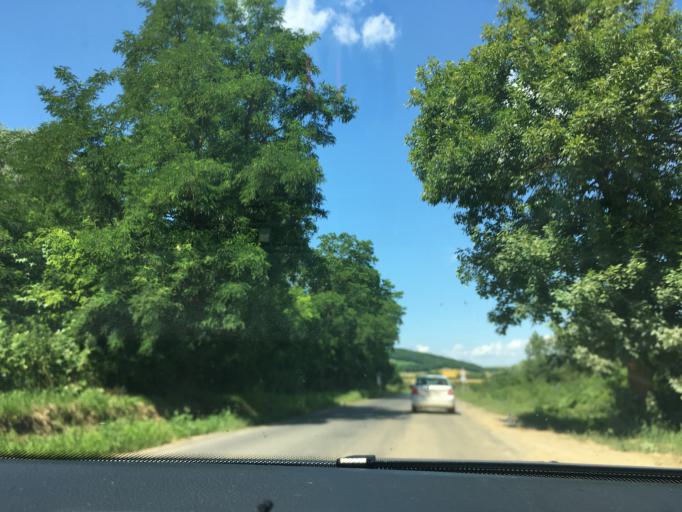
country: HU
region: Borsod-Abauj-Zemplen
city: Tarcal
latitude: 48.1495
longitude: 21.3662
